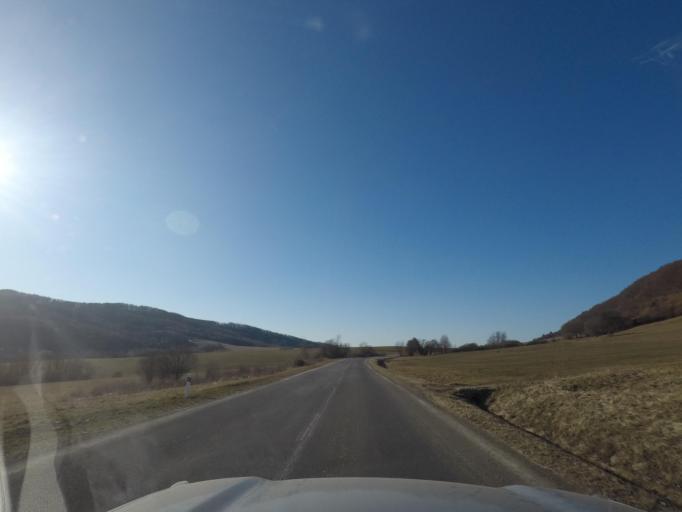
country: SK
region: Presovsky
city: Medzilaborce
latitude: 49.2307
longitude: 21.9598
